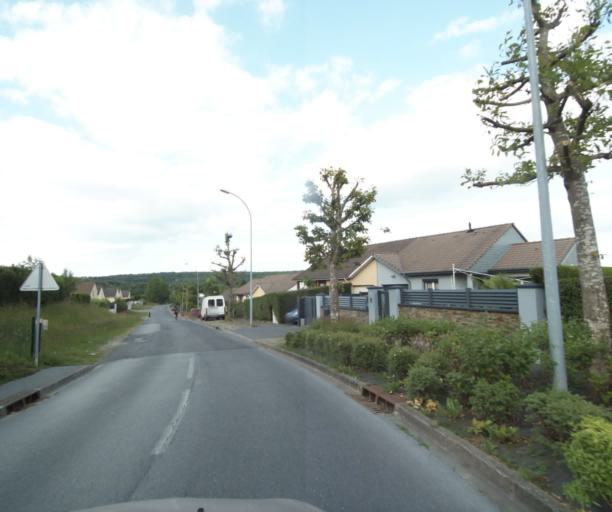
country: FR
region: Champagne-Ardenne
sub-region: Departement des Ardennes
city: Montcy-Notre-Dame
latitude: 49.7909
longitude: 4.7244
